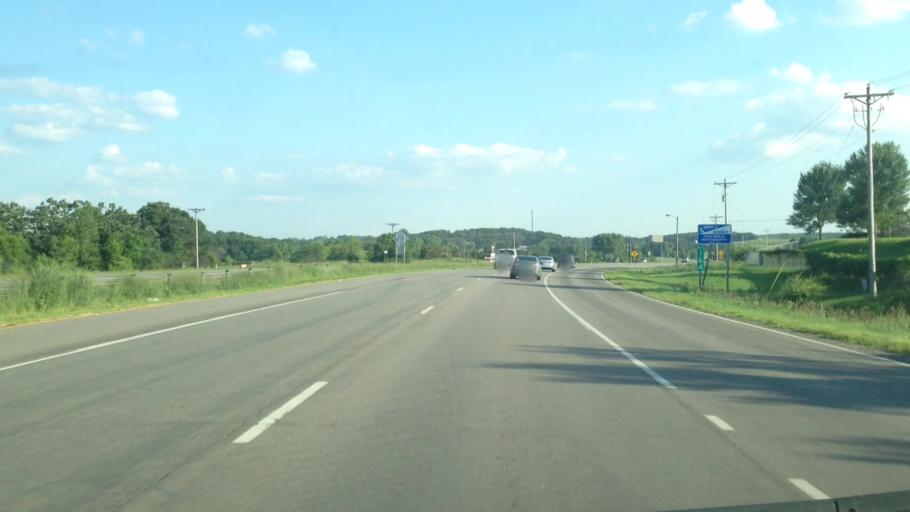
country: US
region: Minnesota
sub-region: Sherburne County
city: Elk River
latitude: 45.3736
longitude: -93.5635
